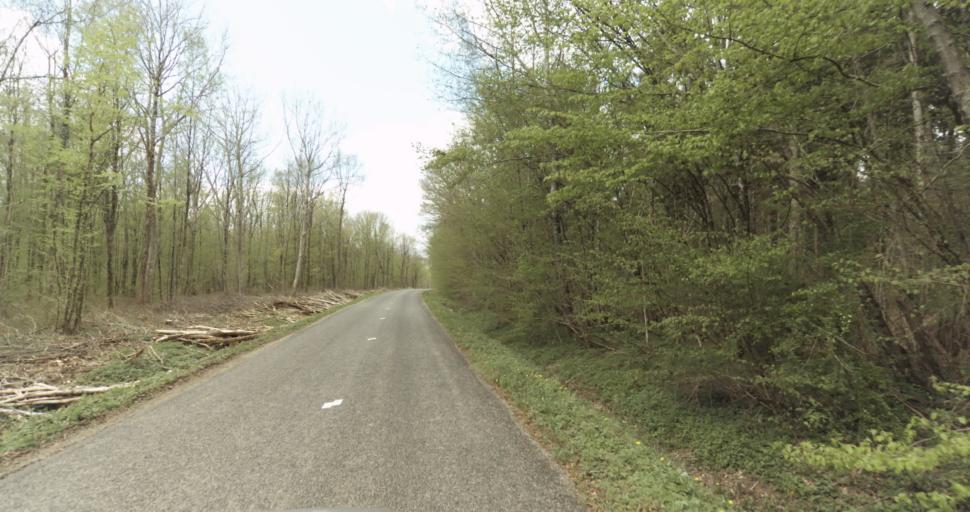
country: FR
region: Franche-Comte
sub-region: Departement du Jura
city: Champvans
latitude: 47.1643
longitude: 5.4505
